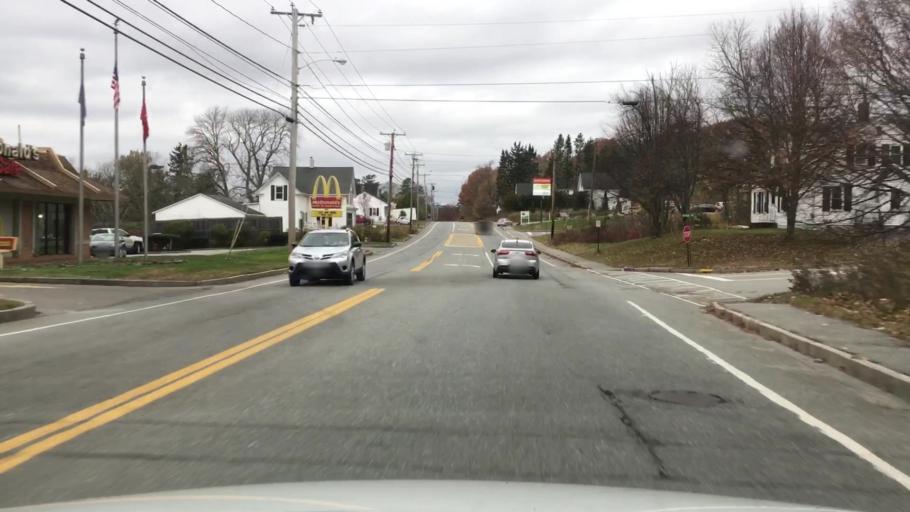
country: US
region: Maine
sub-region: Hancock County
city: Bucksport
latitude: 44.5700
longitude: -68.7762
